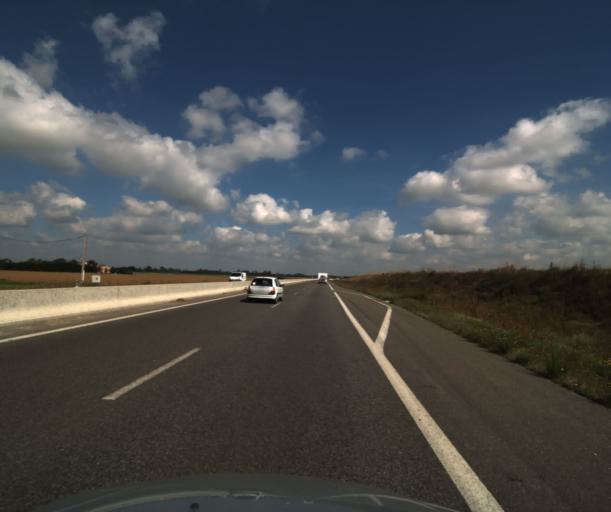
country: FR
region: Midi-Pyrenees
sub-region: Departement de la Haute-Garonne
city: Vernet
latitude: 43.4343
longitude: 1.4164
